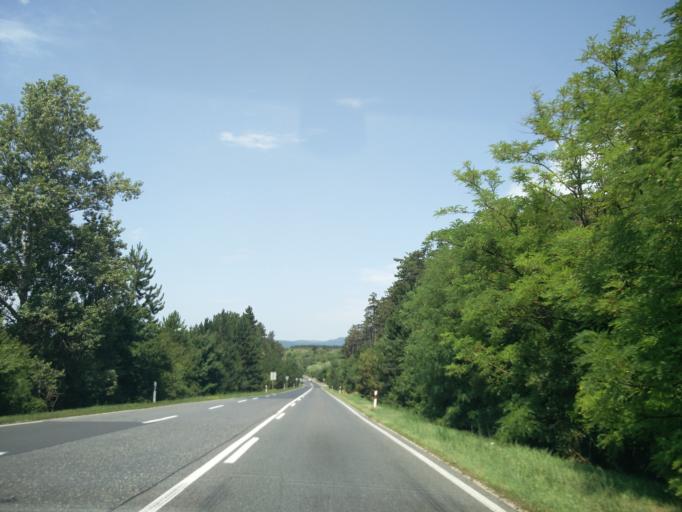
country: HU
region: Veszprem
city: Veszprem
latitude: 47.0930
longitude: 17.8764
